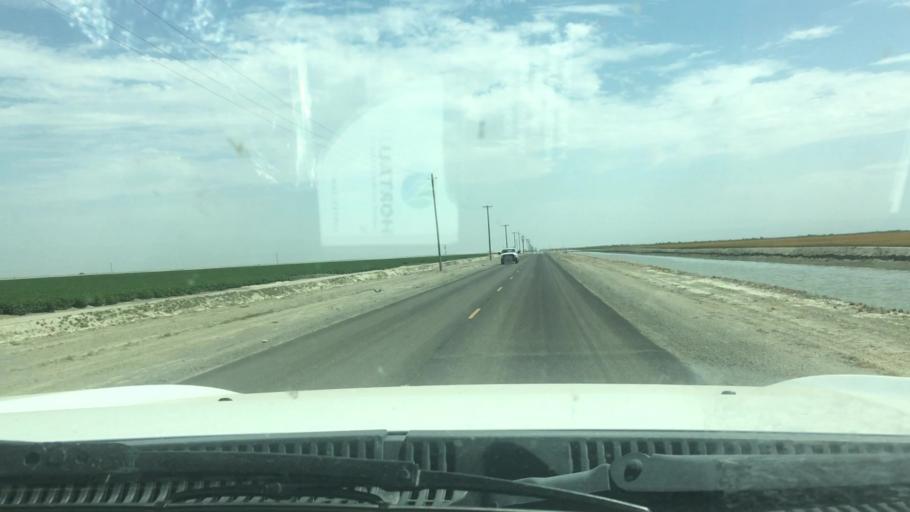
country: US
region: California
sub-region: Tulare County
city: Alpaugh
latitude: 35.8831
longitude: -119.5735
